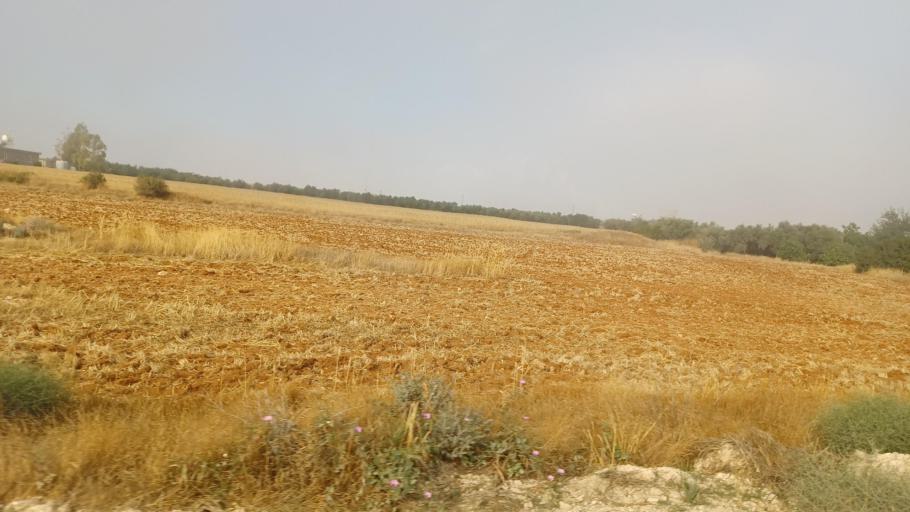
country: CY
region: Ammochostos
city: Acheritou
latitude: 35.1026
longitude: 33.8799
